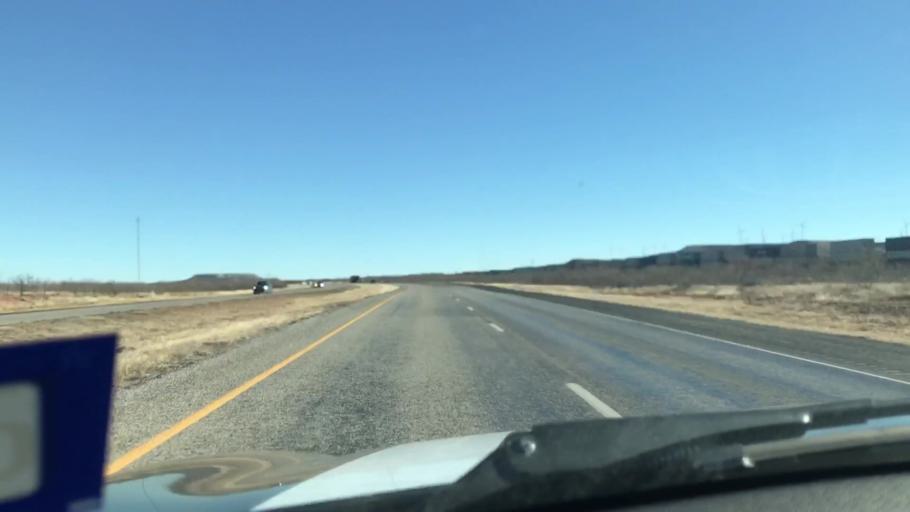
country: US
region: Texas
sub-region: Garza County
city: Post
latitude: 32.9895
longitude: -101.1400
